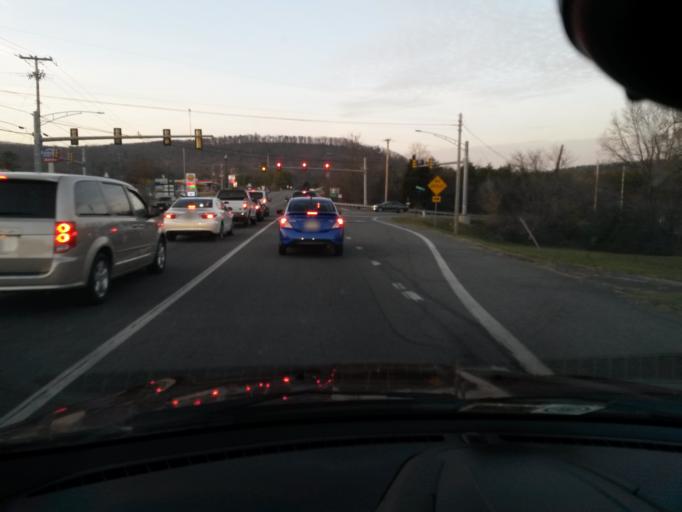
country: US
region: Virginia
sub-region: Roanoke County
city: Hollins
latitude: 37.3567
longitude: -79.9560
